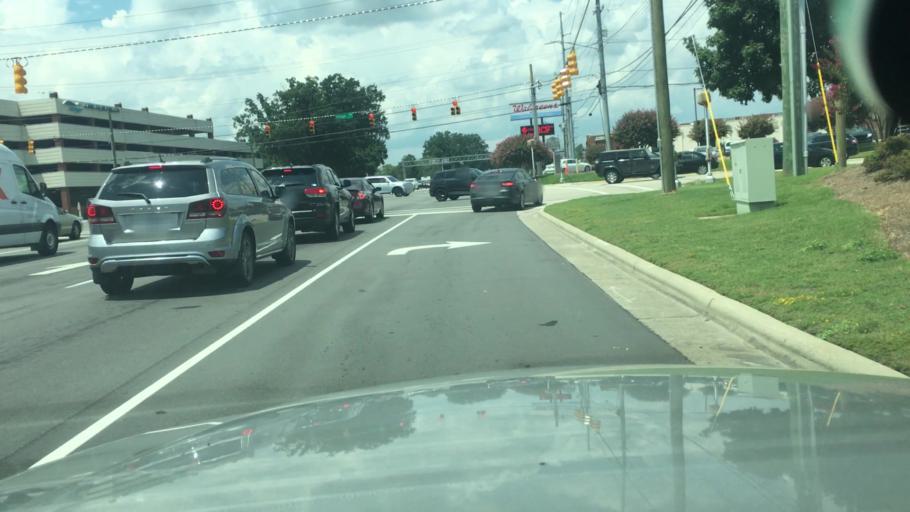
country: US
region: North Carolina
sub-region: Cumberland County
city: Fayetteville
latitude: 35.0303
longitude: -78.9299
